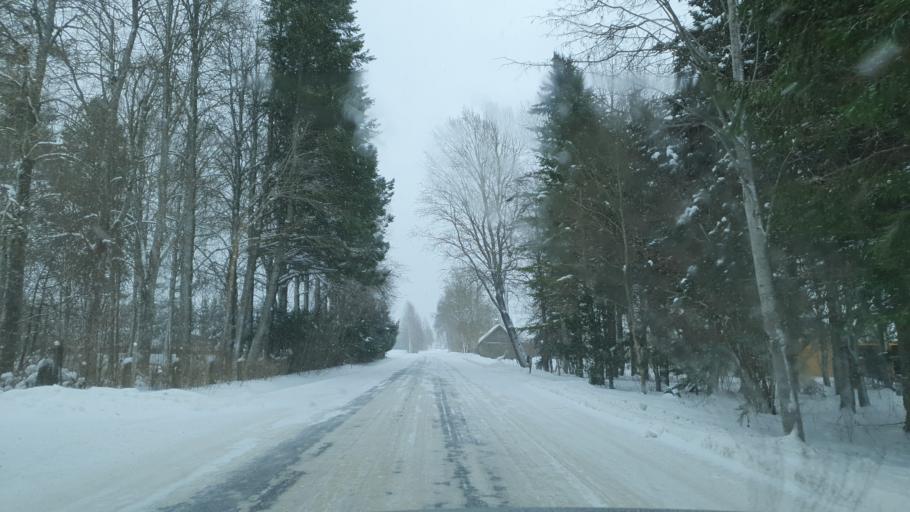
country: EE
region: Jogevamaa
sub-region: Tabivere vald
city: Tabivere
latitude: 58.5746
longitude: 26.7689
